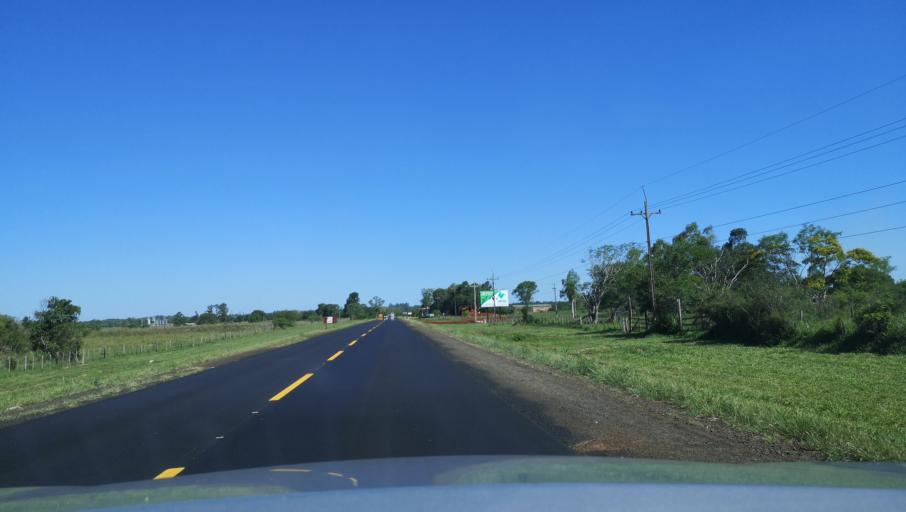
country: PY
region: Itapua
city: Carmen del Parana
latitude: -27.1405
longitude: -56.2713
